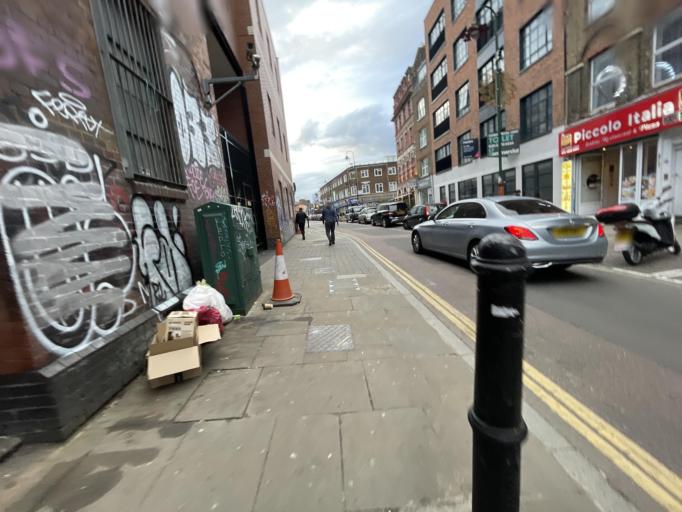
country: GB
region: England
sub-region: Greater London
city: Bethnal Green
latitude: 51.5170
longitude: -0.0701
